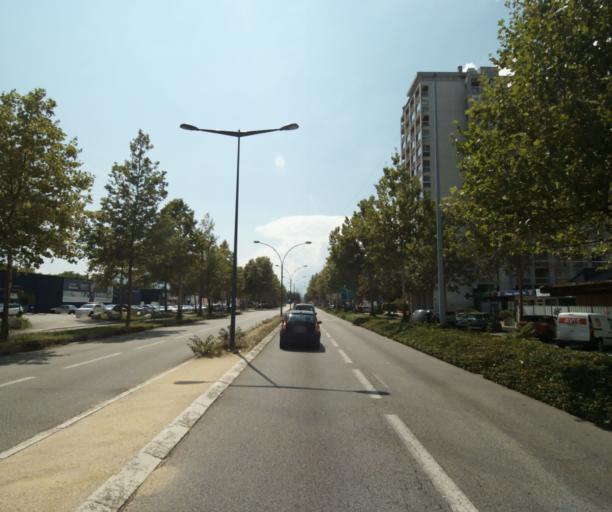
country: FR
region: Rhone-Alpes
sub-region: Departement de l'Isere
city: Grenoble
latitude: 45.1619
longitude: 5.7102
